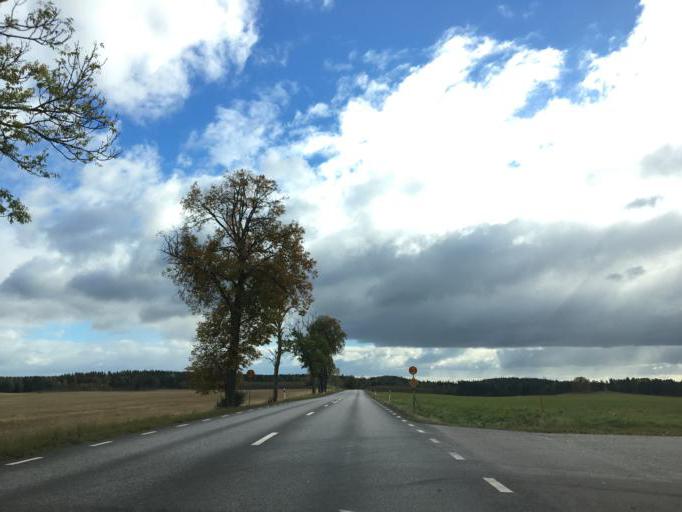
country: SE
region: Soedermanland
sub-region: Katrineholms Kommun
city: Katrineholm
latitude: 58.9428
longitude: 16.3909
